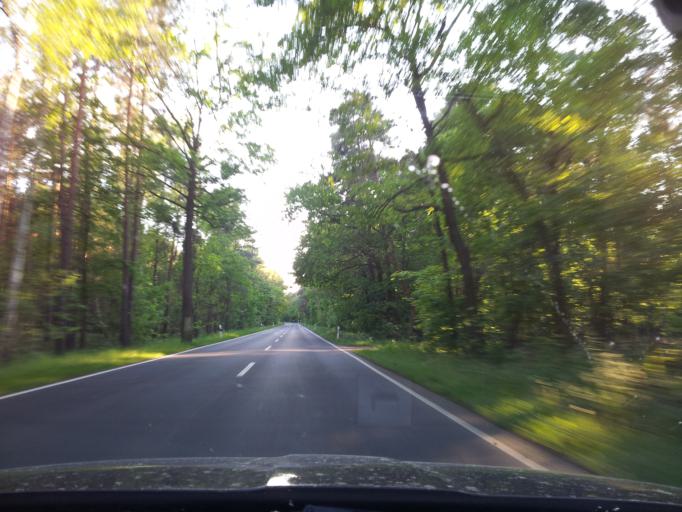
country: DE
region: Brandenburg
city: Luckenwalde
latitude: 52.0580
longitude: 13.1535
